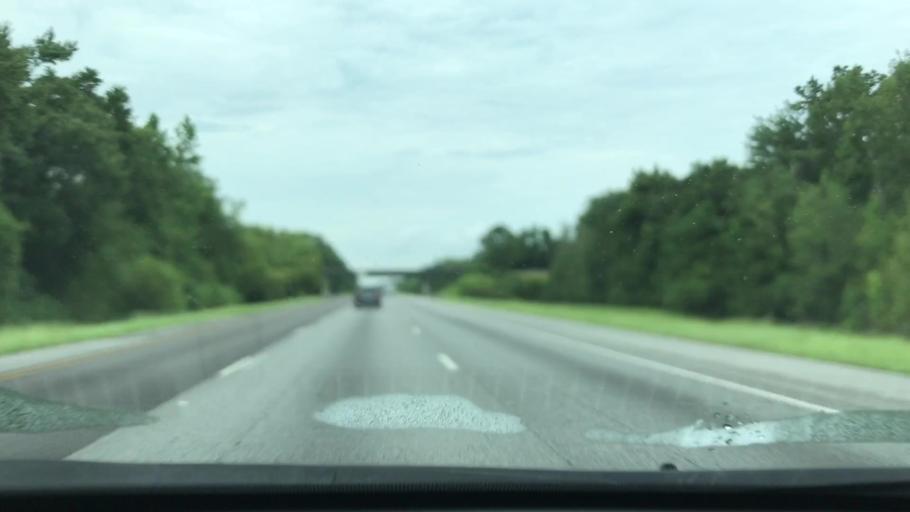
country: US
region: Georgia
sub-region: Liberty County
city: Midway
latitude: 31.6980
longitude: -81.3916
